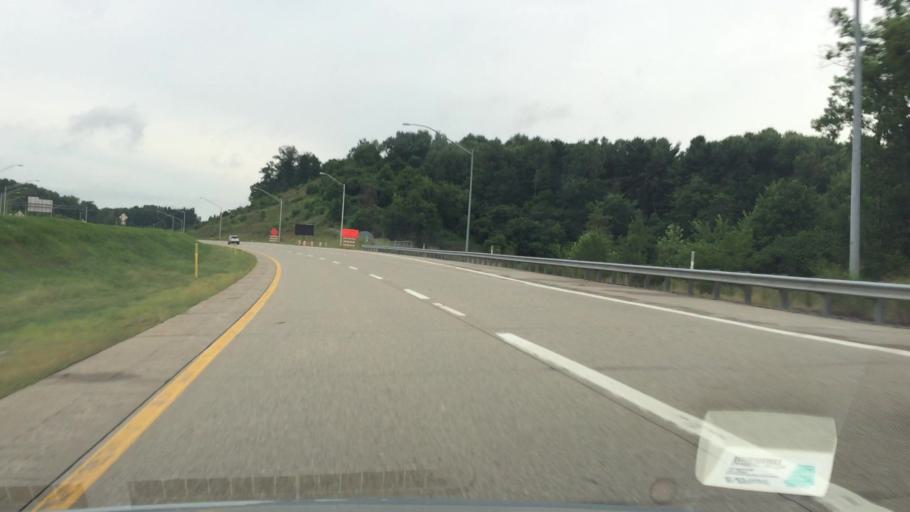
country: US
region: Pennsylvania
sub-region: Allegheny County
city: Imperial
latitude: 40.4820
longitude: -80.2771
